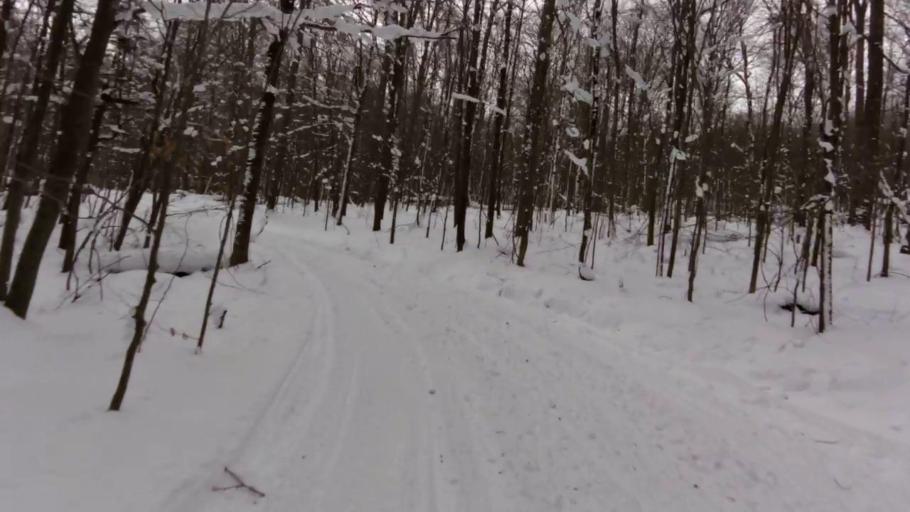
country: US
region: New York
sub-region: Cattaraugus County
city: Salamanca
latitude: 42.0624
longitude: -78.7792
